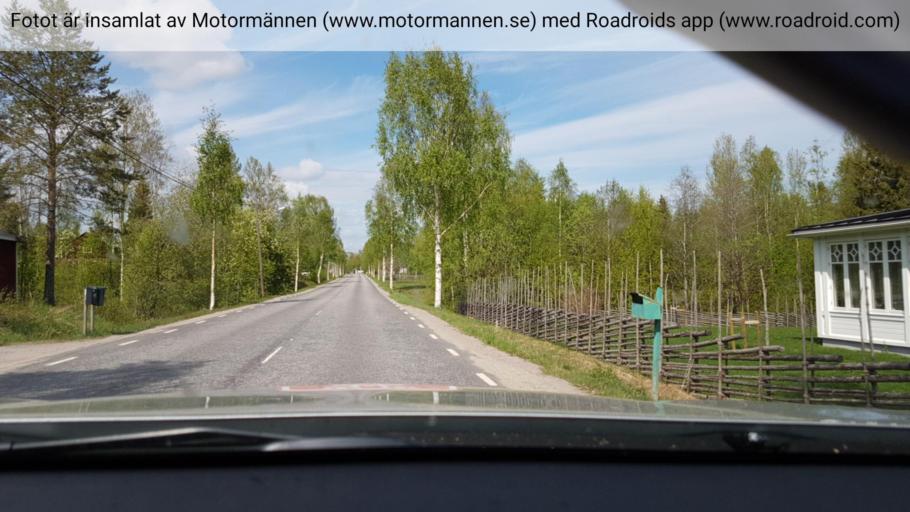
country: SE
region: Vaesterbotten
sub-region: Vannas Kommun
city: Vannasby
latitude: 63.8665
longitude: 19.8979
